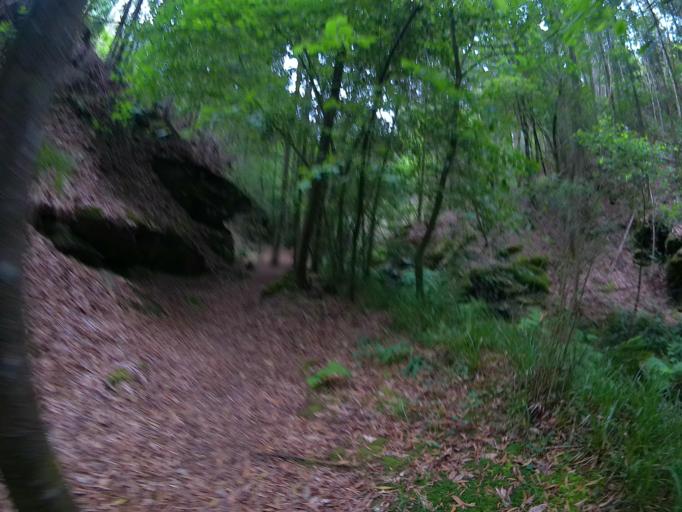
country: PT
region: Aveiro
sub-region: Albergaria-A-Velha
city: Branca
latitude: 40.7445
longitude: -8.4349
